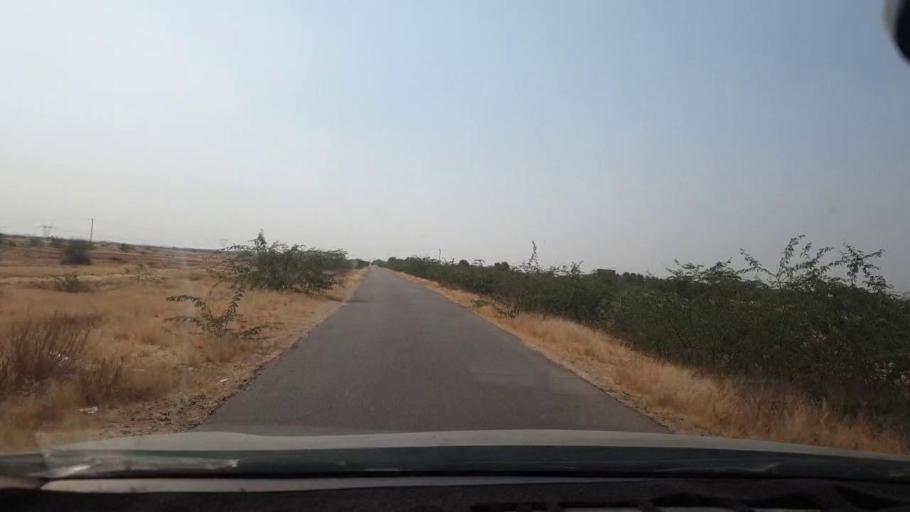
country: PK
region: Sindh
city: Malir Cantonment
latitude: 25.1231
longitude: 67.2199
